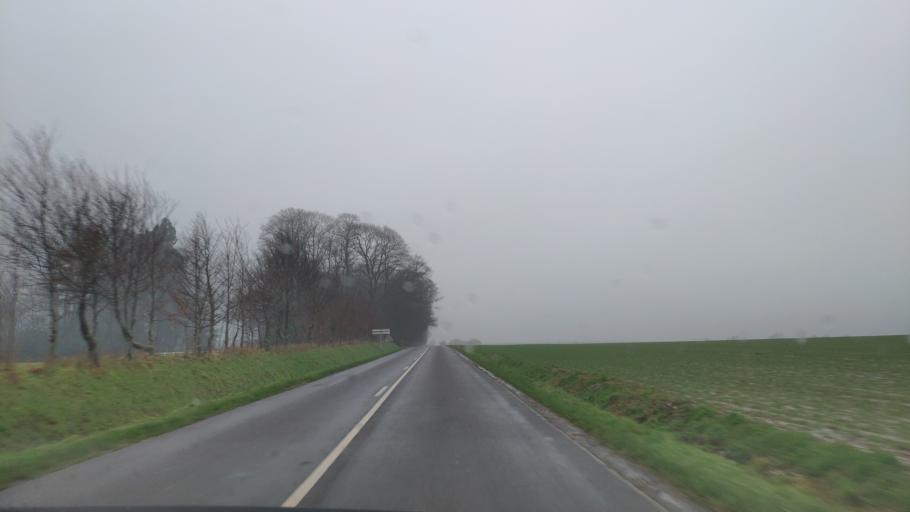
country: FR
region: Haute-Normandie
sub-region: Departement de la Seine-Maritime
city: Doudeville
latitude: 49.7656
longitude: 0.7551
